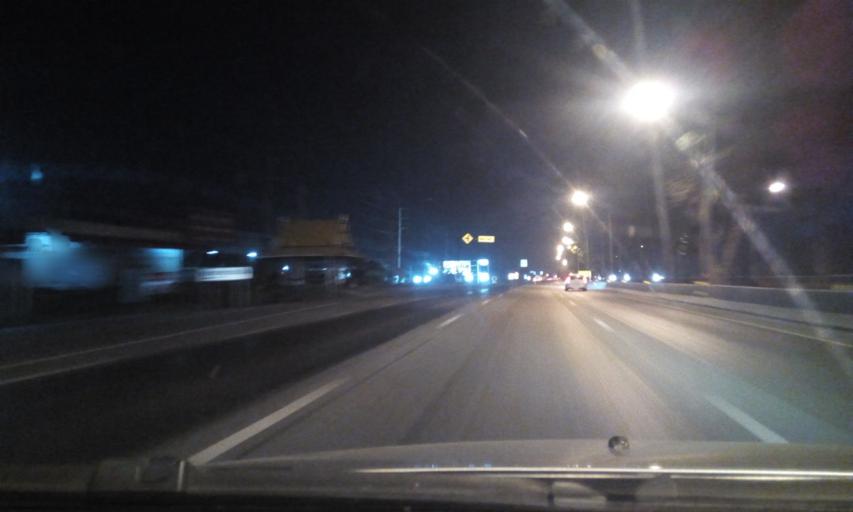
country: TH
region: Sing Buri
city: Phrom Buri
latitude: 14.7528
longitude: 100.4537
